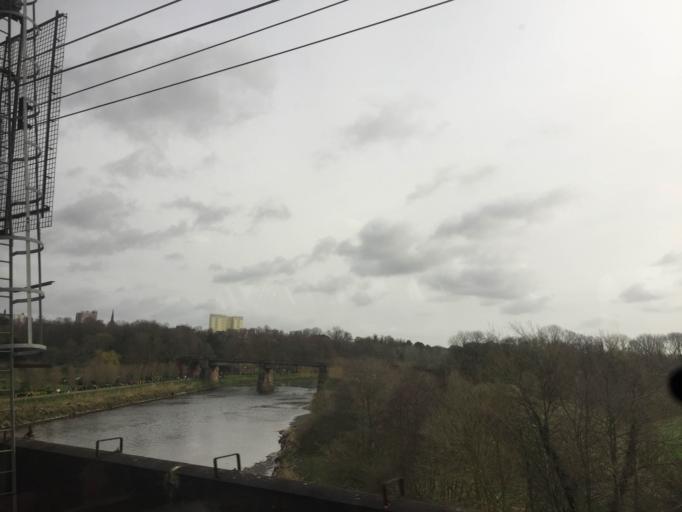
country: GB
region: England
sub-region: Lancashire
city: Preston
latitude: 53.7493
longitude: -2.7059
